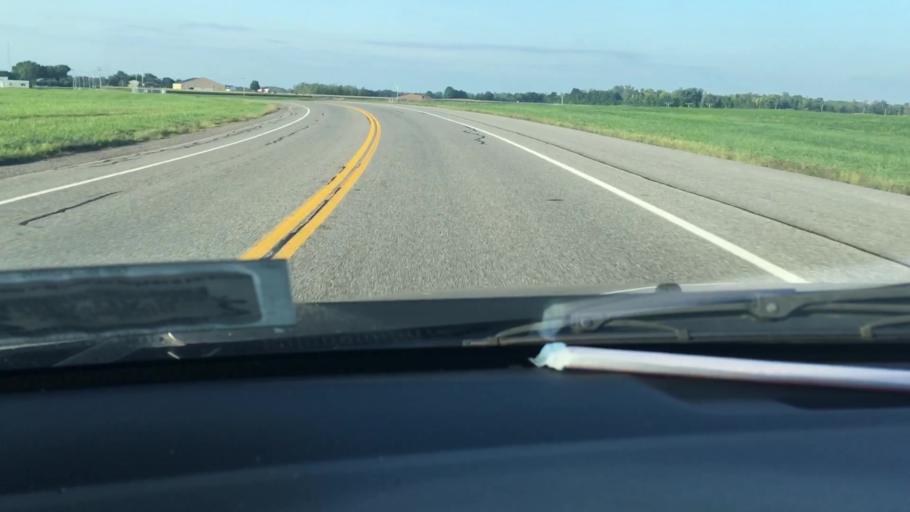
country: US
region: New York
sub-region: Genesee County
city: Batavia
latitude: 43.0334
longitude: -78.1525
